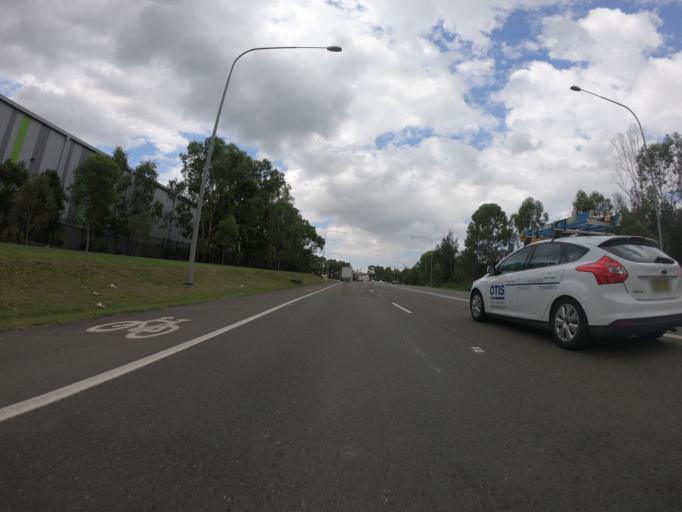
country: AU
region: New South Wales
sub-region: Blacktown
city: Mount Druitt
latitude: -33.8155
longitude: 150.7798
